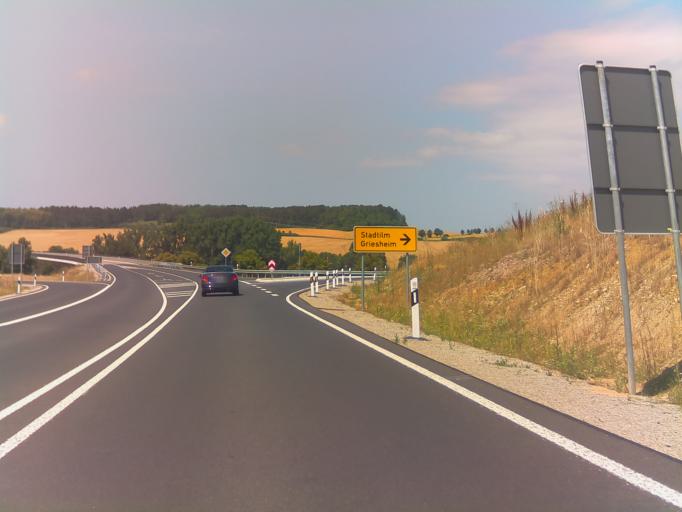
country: DE
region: Thuringia
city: Stadtilm
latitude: 50.7591
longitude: 11.0599
